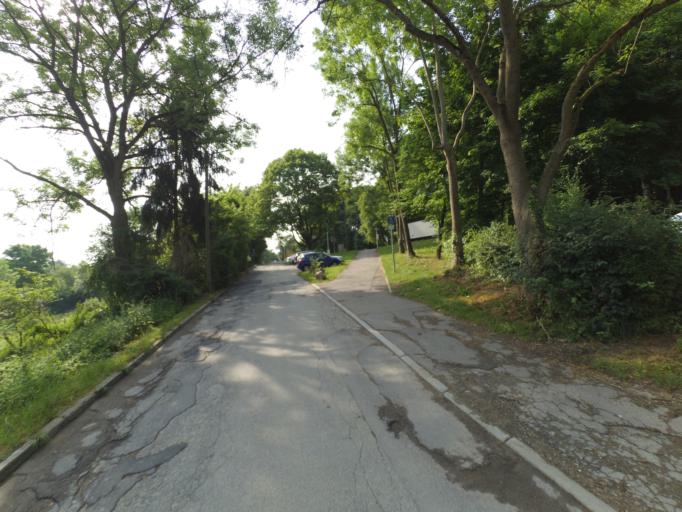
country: DE
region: Baden-Wuerttemberg
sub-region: Tuebingen Region
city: Ulm
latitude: 48.4100
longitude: 9.9989
